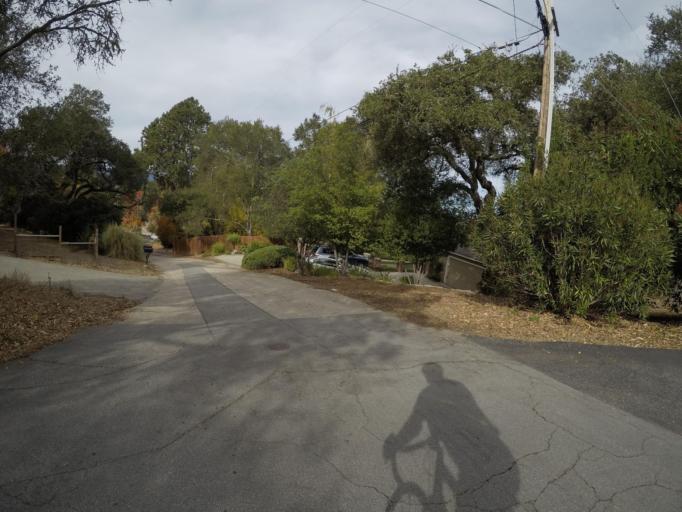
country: US
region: California
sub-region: Santa Cruz County
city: Scotts Valley
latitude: 37.0583
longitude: -121.9952
